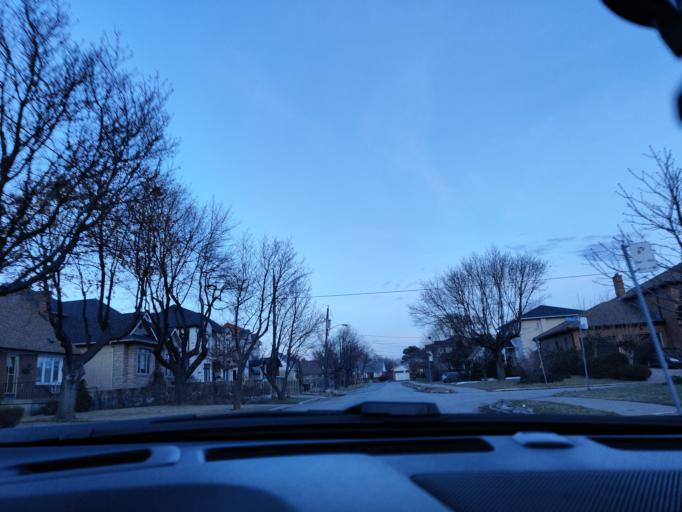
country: CA
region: Ontario
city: Toronto
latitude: 43.7183
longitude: -79.4520
